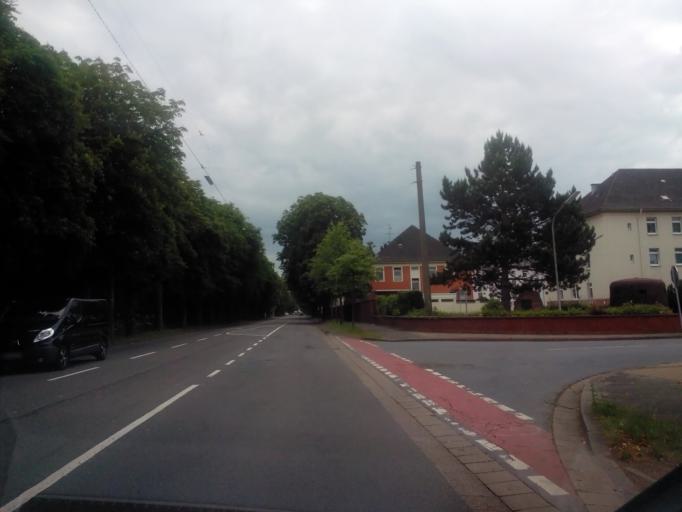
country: DE
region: Saarland
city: Saarlouis
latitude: 49.3163
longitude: 6.7375
